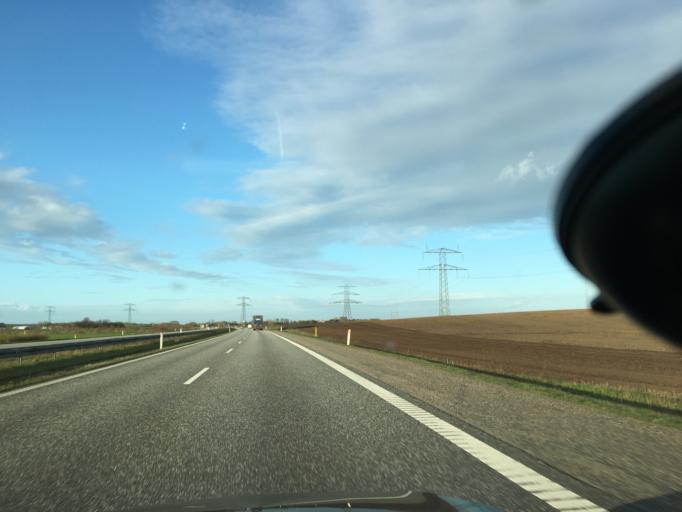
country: DK
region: North Denmark
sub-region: Rebild Kommune
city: Stovring
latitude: 56.8694
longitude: 9.7902
